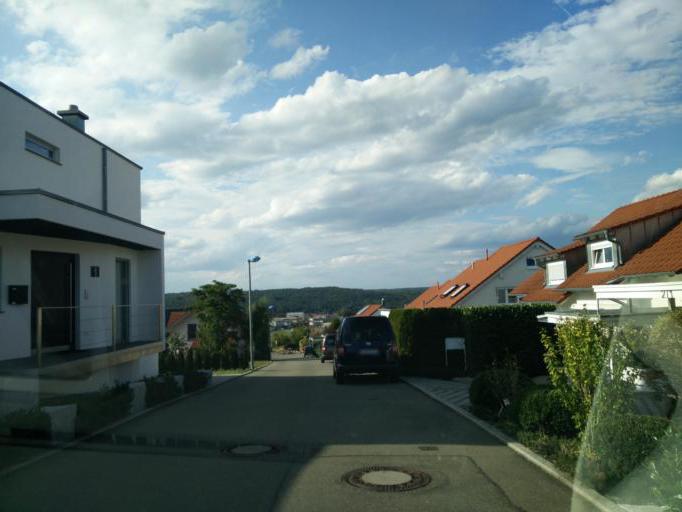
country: DE
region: Baden-Wuerttemberg
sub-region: Tuebingen Region
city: Kirchentellinsfurt
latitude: 48.5295
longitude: 9.1597
